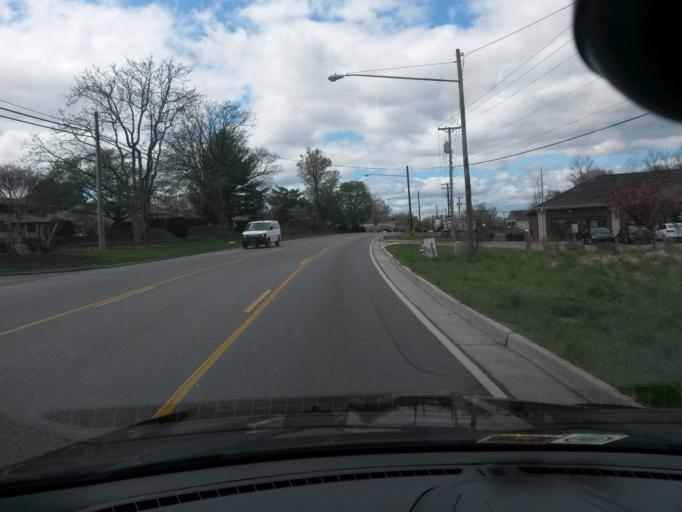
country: US
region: Virginia
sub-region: City of Lynchburg
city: West Lynchburg
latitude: 37.4004
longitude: -79.2024
